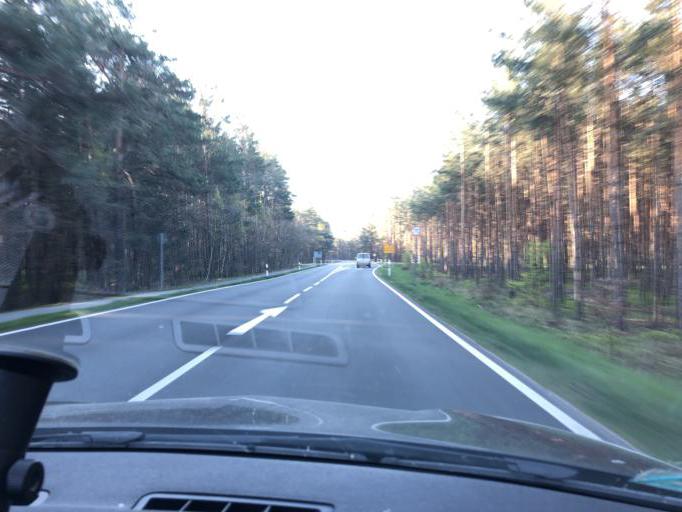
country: DE
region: Saxony
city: Rietschen
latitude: 51.3485
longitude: 14.8036
